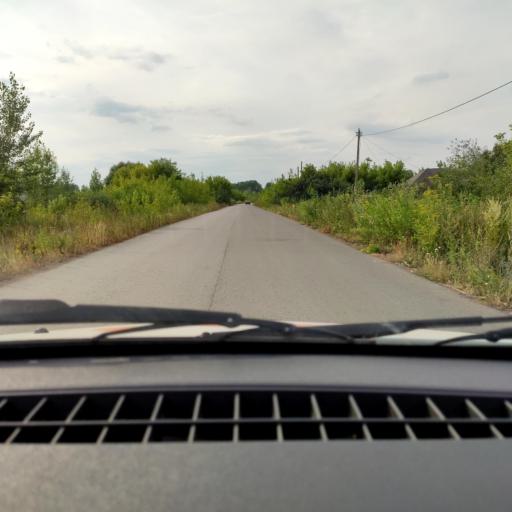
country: RU
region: Bashkortostan
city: Blagoveshchensk
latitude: 54.9018
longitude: 56.0144
